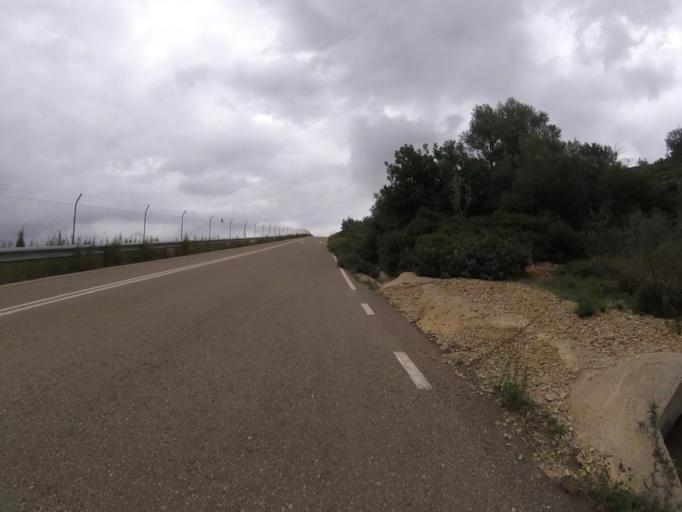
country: ES
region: Valencia
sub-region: Provincia de Castello
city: Benlloch
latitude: 40.1870
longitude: 0.0472
